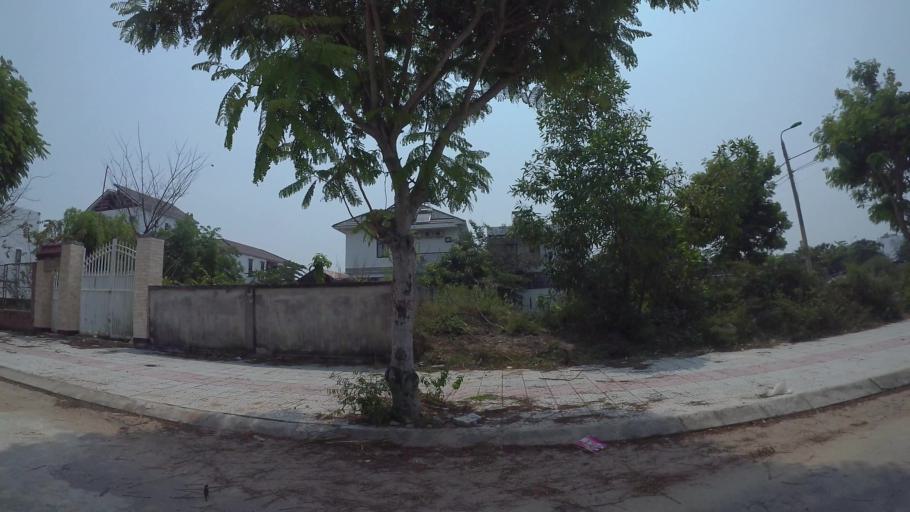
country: VN
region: Da Nang
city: Cam Le
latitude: 16.0106
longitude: 108.2155
